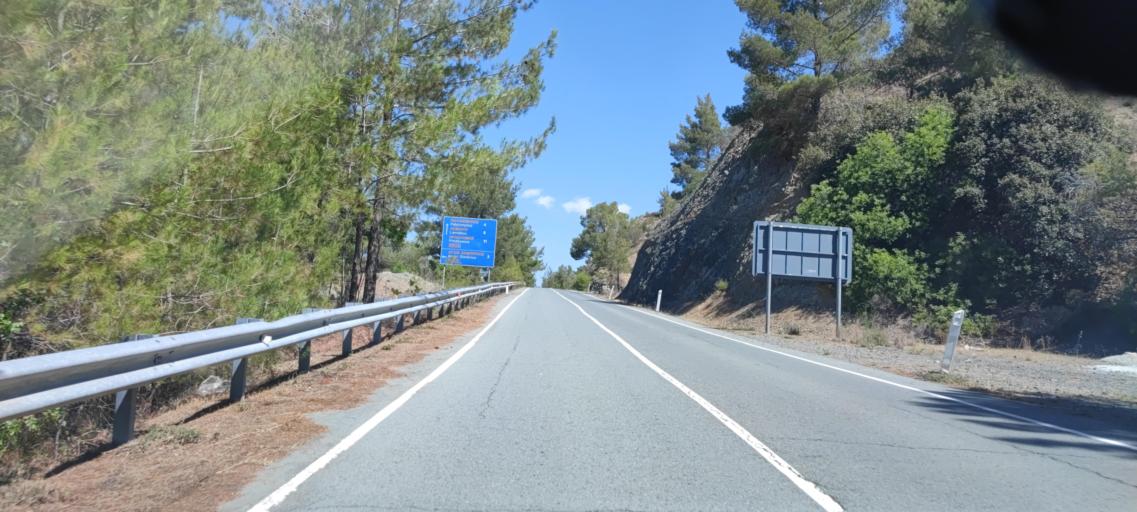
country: CY
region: Lefkosia
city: Kakopetria
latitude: 34.9146
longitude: 32.8152
